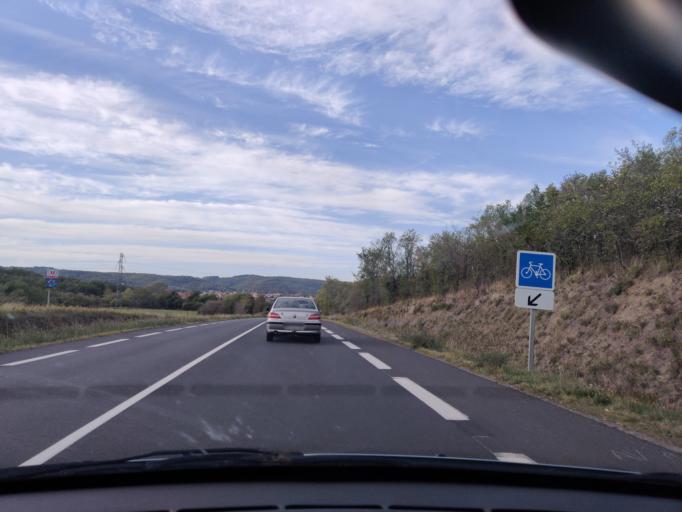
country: FR
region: Auvergne
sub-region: Departement du Puy-de-Dome
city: Mozac
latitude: 45.9089
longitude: 3.0850
